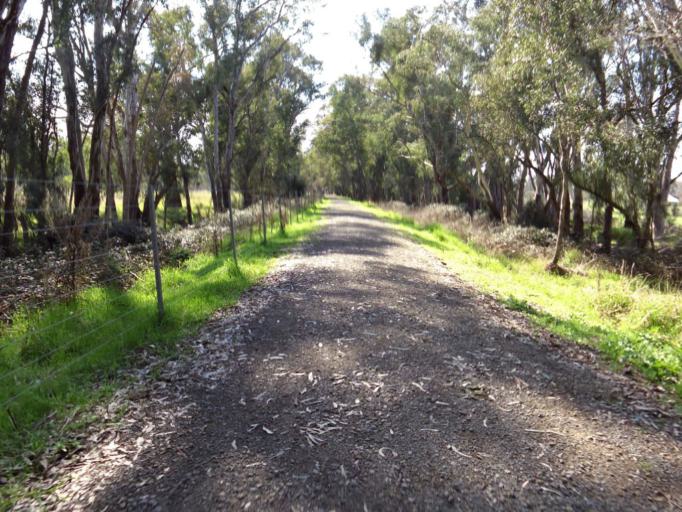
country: AU
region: Victoria
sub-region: Murrindindi
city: Alexandra
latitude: -37.1567
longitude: 145.5725
